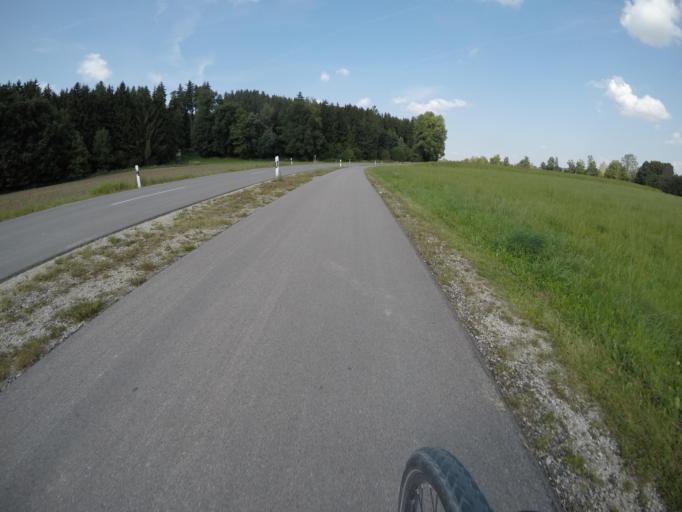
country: DE
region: Bavaria
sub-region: Swabia
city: Kuhlenthal
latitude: 48.5713
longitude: 10.8225
